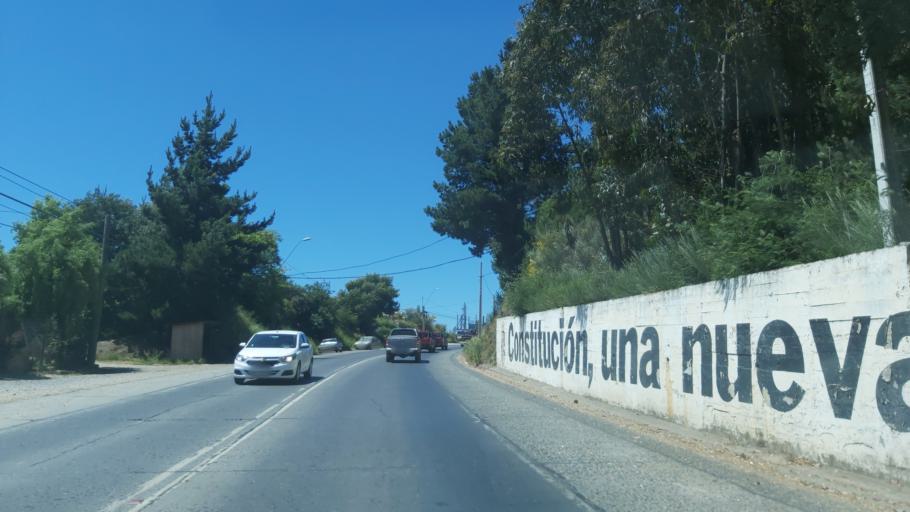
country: CL
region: Maule
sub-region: Provincia de Talca
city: Constitucion
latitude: -35.3506
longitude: -72.4115
